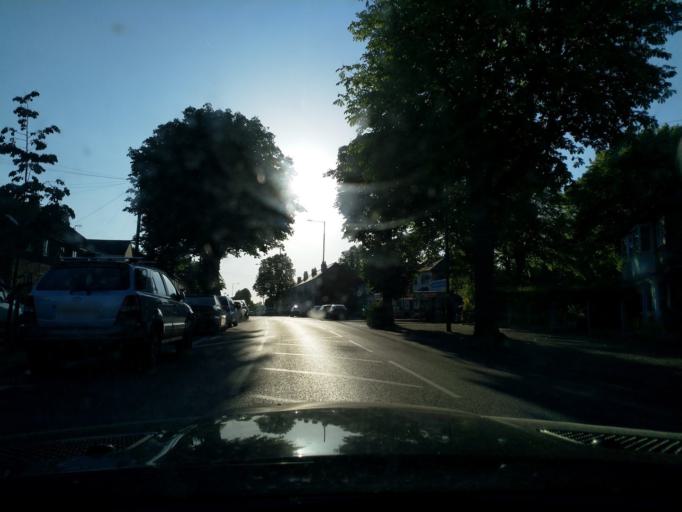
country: GB
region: England
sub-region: City and Borough of Birmingham
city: Acocks Green
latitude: 52.4423
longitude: -1.8452
